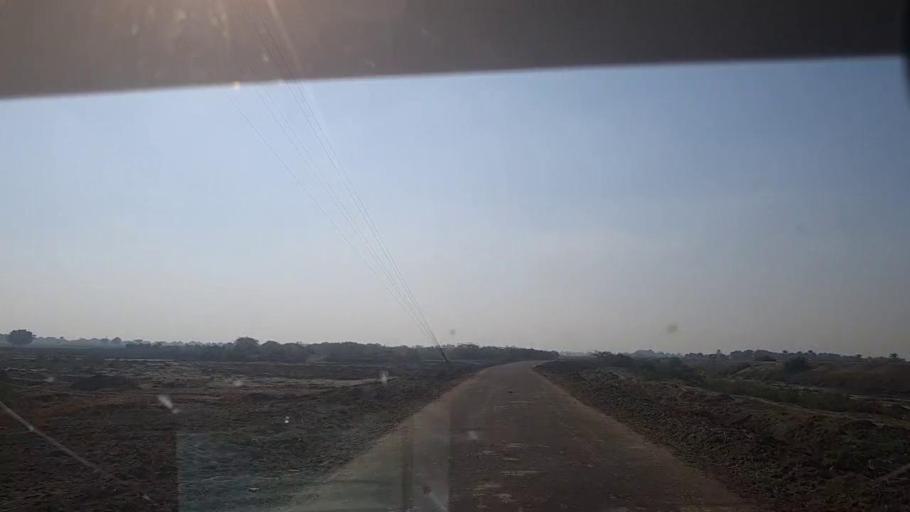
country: PK
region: Sindh
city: Gambat
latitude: 27.3840
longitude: 68.5883
